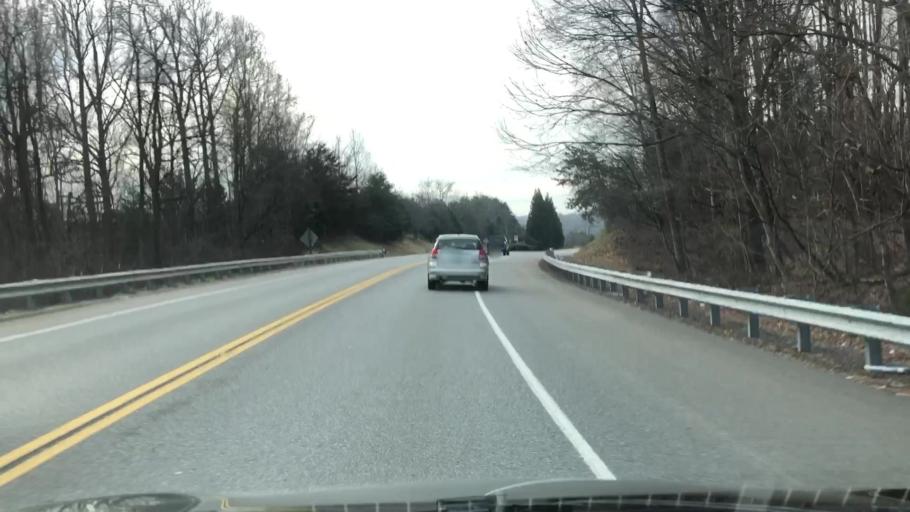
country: US
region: Virginia
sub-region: City of Lynchburg
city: West Lynchburg
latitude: 37.4213
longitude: -79.2313
